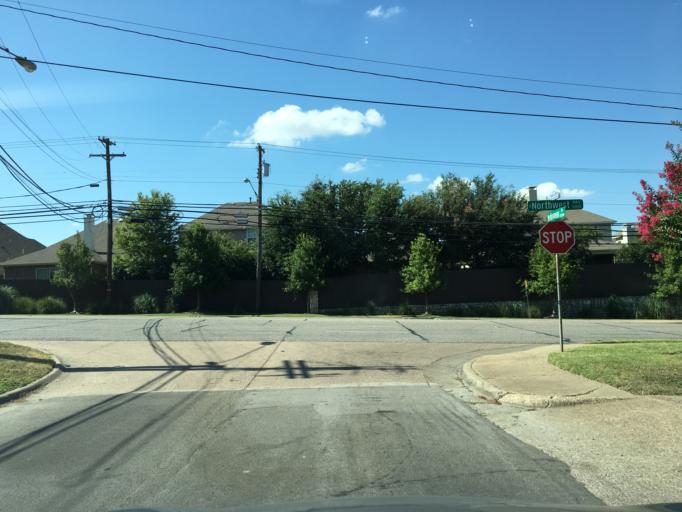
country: US
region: Texas
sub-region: Dallas County
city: Garland
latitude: 32.8649
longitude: -96.6972
